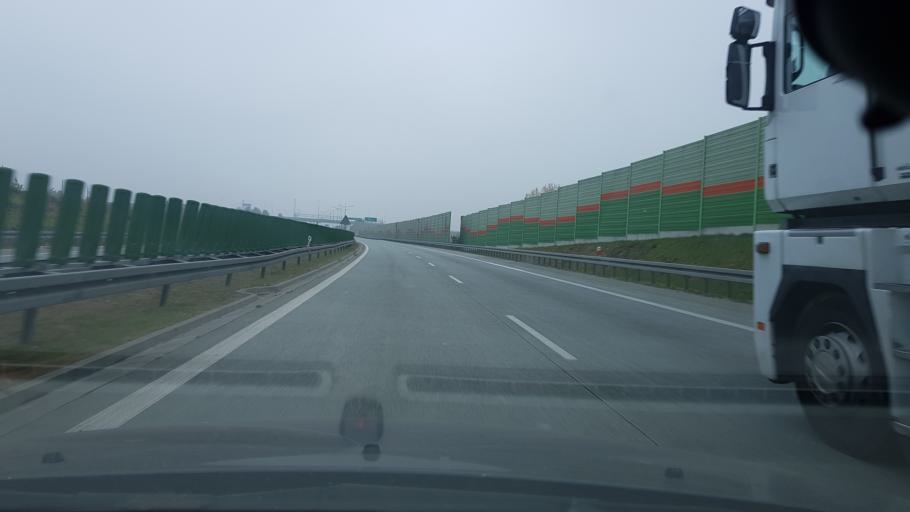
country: PL
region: Lodz Voivodeship
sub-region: Powiat rawski
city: Rawa Mazowiecka
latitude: 51.7679
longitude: 20.2720
